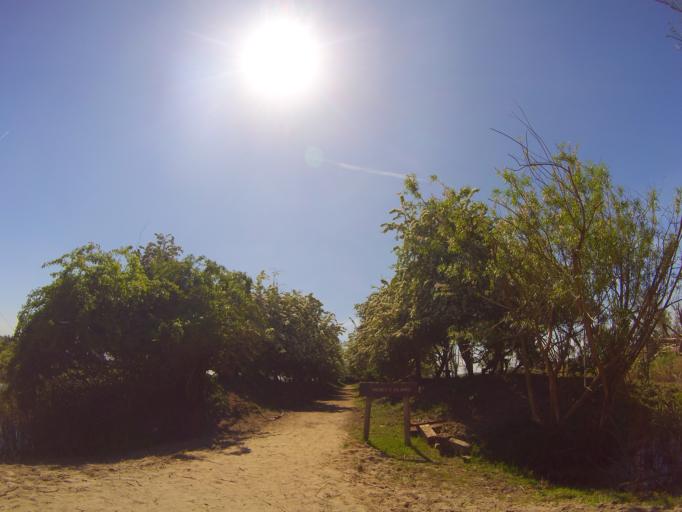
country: NL
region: Flevoland
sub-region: Gemeente Lelystad
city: Lelystad
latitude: 52.4491
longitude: 5.4054
